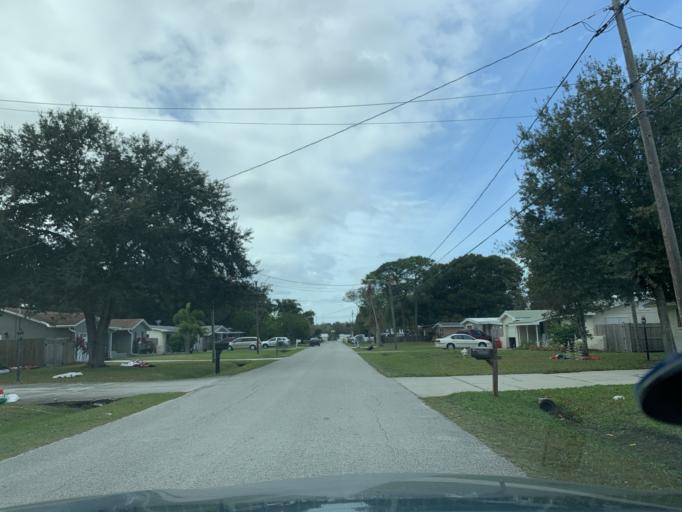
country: US
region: Florida
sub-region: Pinellas County
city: Ridgecrest
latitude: 27.8858
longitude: -82.7889
